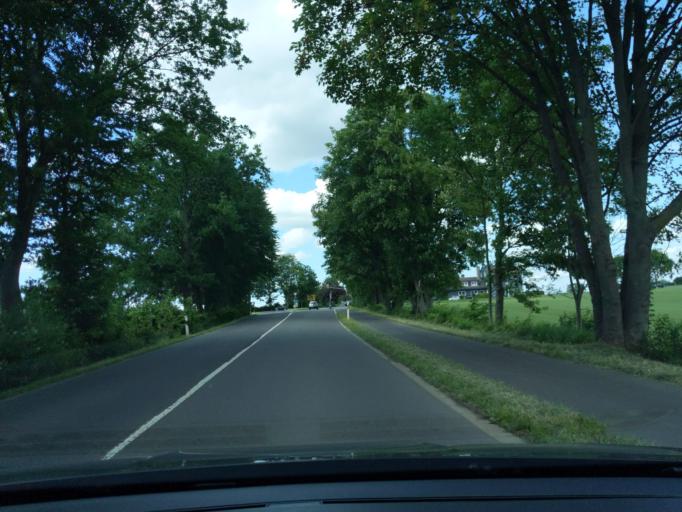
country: DE
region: North Rhine-Westphalia
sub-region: Regierungsbezirk Dusseldorf
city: Erkrath
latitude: 51.2598
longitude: 6.9032
